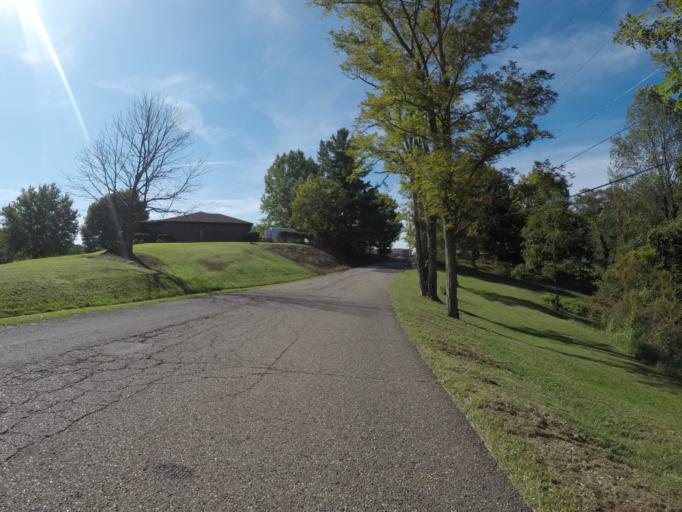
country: US
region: West Virginia
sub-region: Cabell County
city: Huntington
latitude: 38.4603
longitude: -82.4606
